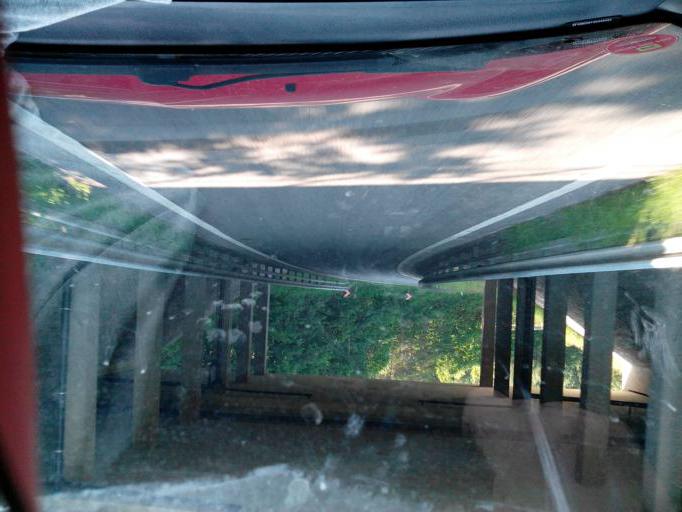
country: AT
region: Lower Austria
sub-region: Politischer Bezirk Baden
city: Alland
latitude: 48.0602
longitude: 16.0933
